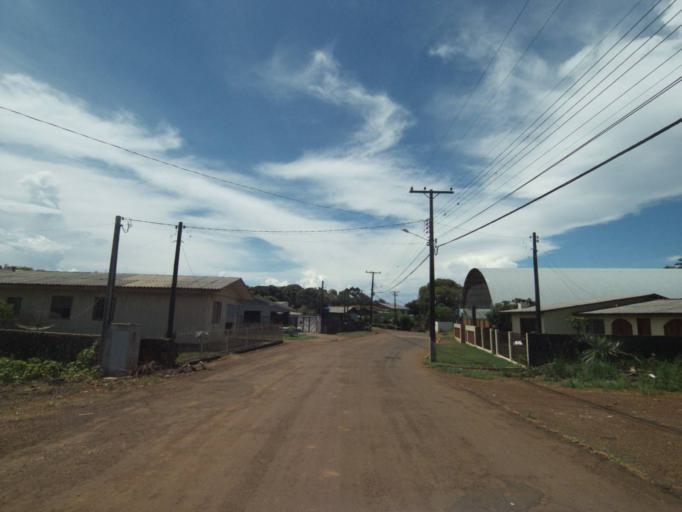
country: BR
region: Parana
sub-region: Guaraniacu
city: Guaraniacu
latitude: -25.0929
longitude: -52.8742
